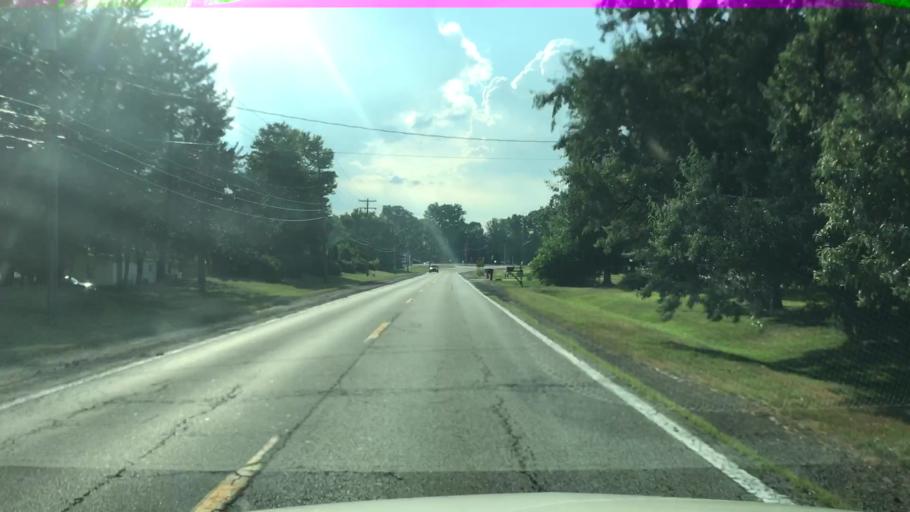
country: US
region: Michigan
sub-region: Macomb County
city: Fraser
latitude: 42.5784
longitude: -82.9676
